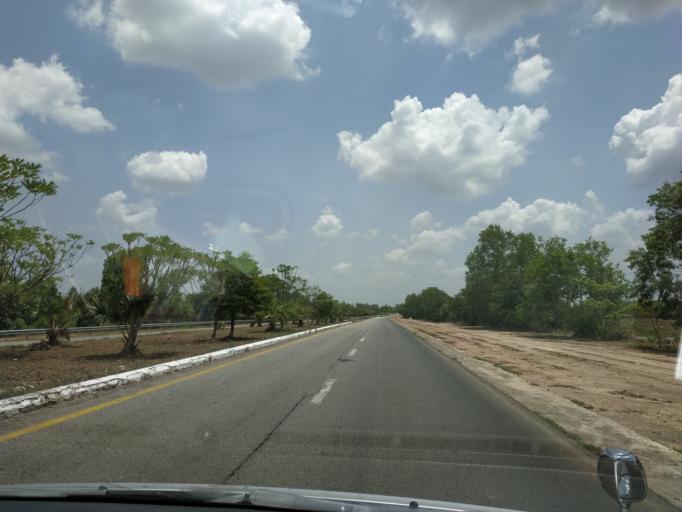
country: MM
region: Bago
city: Thanatpin
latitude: 17.0987
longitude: 96.1781
